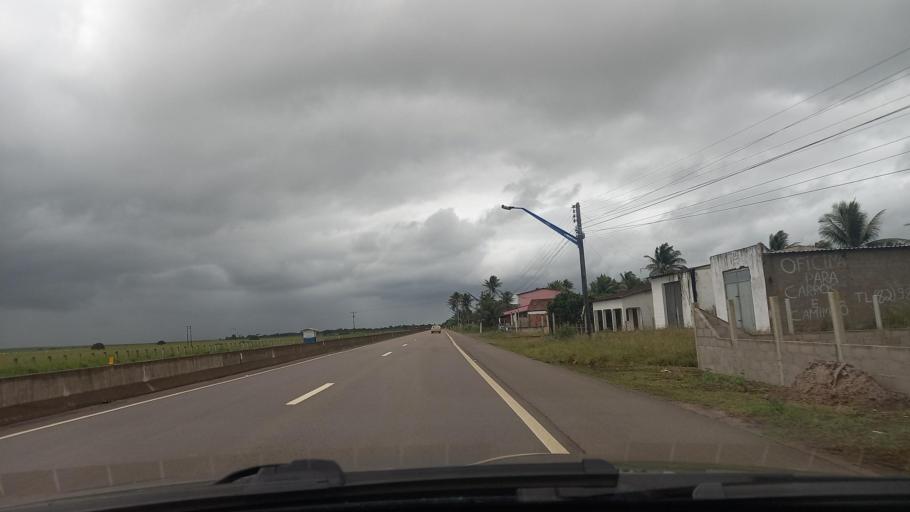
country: BR
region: Alagoas
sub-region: Limoeiro De Anadia
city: Cajueiro
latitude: -9.7439
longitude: -36.4655
